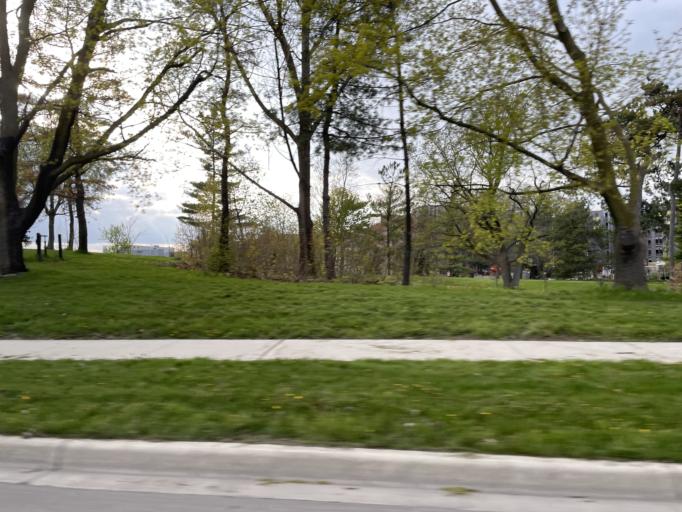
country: CA
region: Ontario
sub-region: Wellington County
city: Guelph
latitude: 43.5285
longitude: -80.2225
